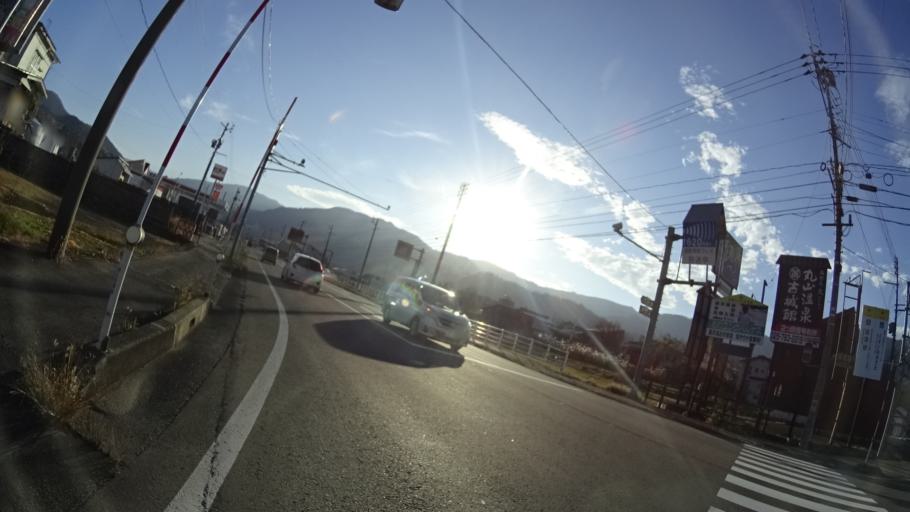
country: JP
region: Niigata
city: Shiozawa
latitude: 36.9896
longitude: 138.8098
